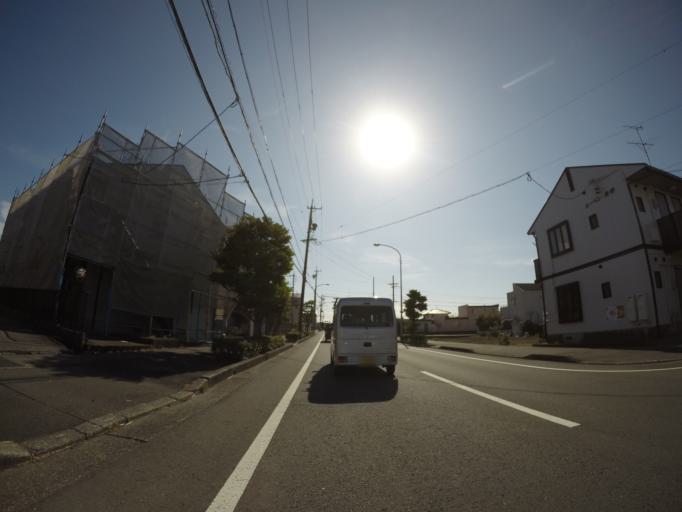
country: JP
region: Shizuoka
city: Shizuoka-shi
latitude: 34.9669
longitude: 138.4229
